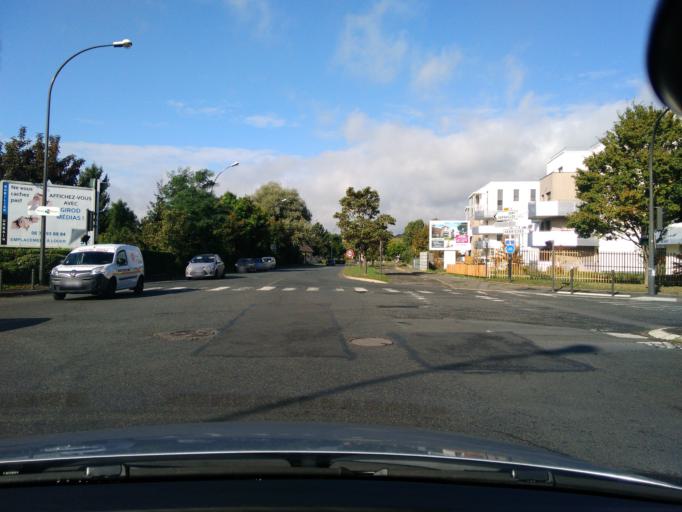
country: FR
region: Ile-de-France
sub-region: Departement de l'Essonne
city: Verrieres-le-Buisson
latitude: 48.7375
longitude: 2.2679
